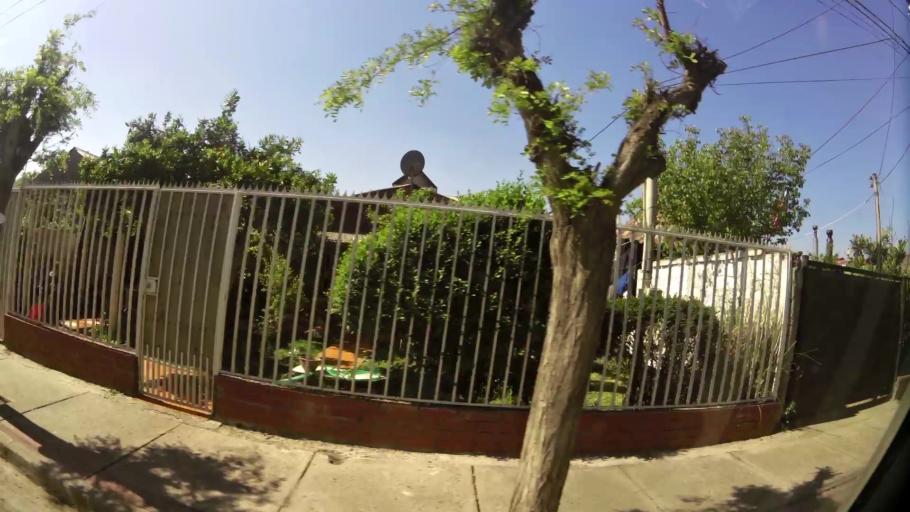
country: CL
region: Santiago Metropolitan
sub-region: Provincia de Talagante
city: Penaflor
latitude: -33.5663
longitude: -70.8076
